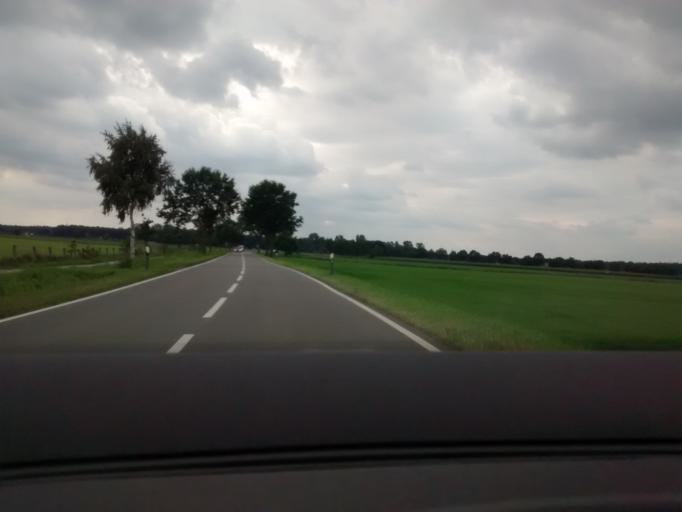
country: DE
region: Lower Saxony
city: Echem
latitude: 53.3271
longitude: 10.5075
